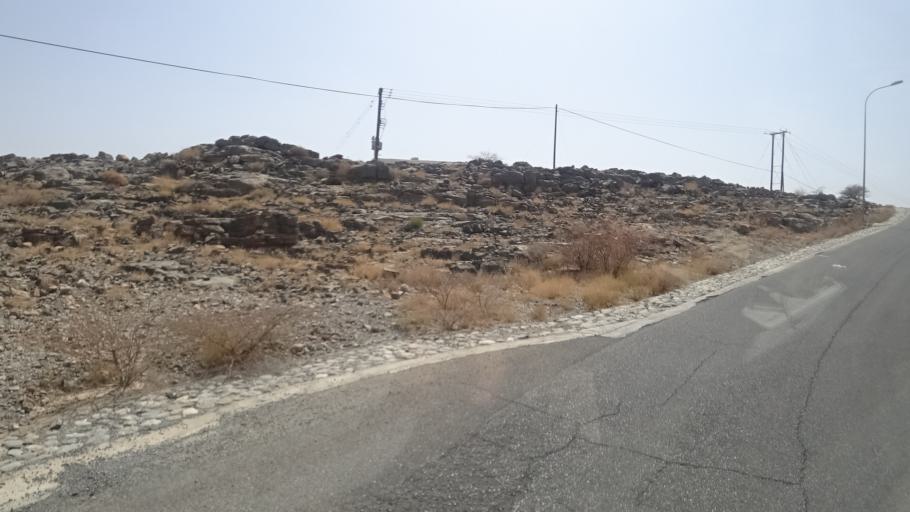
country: OM
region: Muhafazat ad Dakhiliyah
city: Bahla'
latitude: 23.1292
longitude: 57.3058
